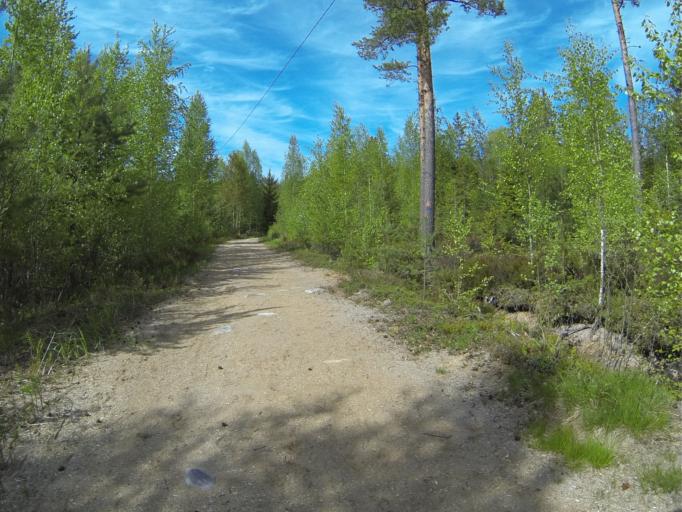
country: FI
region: Varsinais-Suomi
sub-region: Salo
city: Salo
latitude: 60.3884
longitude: 23.1905
